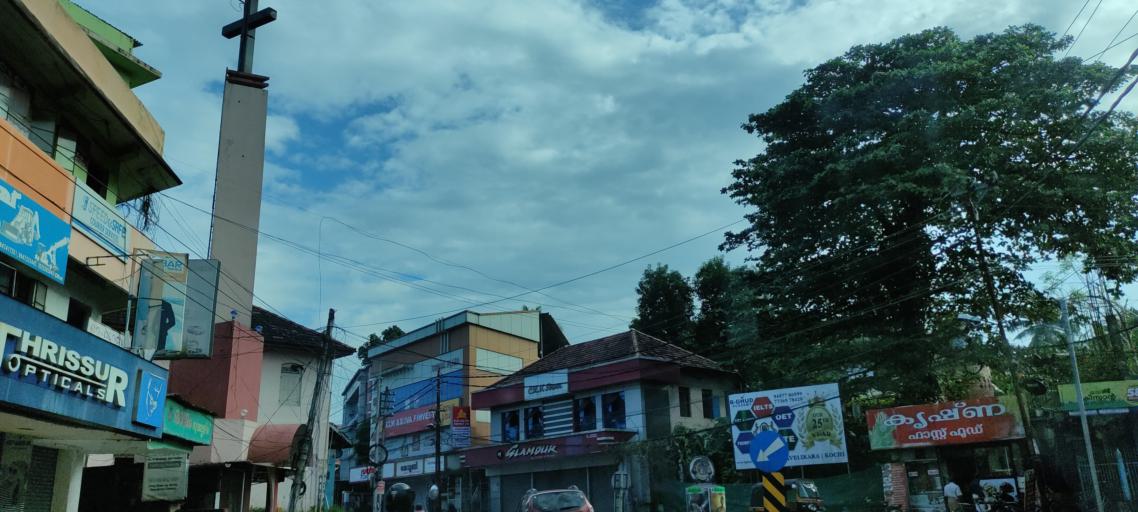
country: IN
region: Kerala
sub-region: Alappuzha
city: Mavelikara
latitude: 9.2511
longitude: 76.5412
